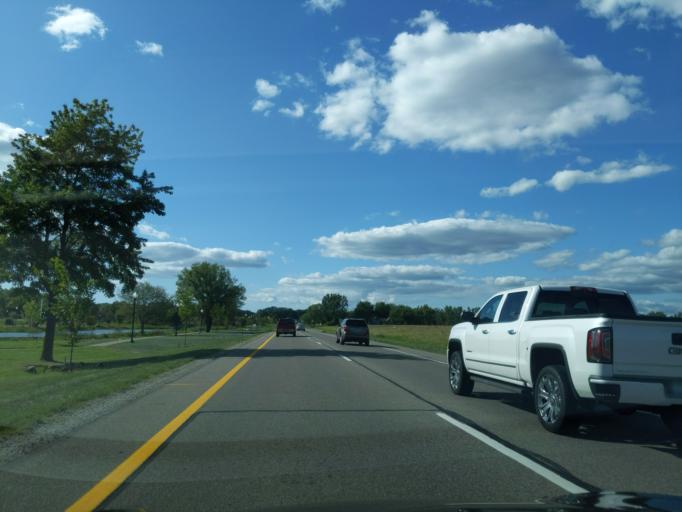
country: US
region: Michigan
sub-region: Muskegon County
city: North Muskegon
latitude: 43.2599
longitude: -86.2414
